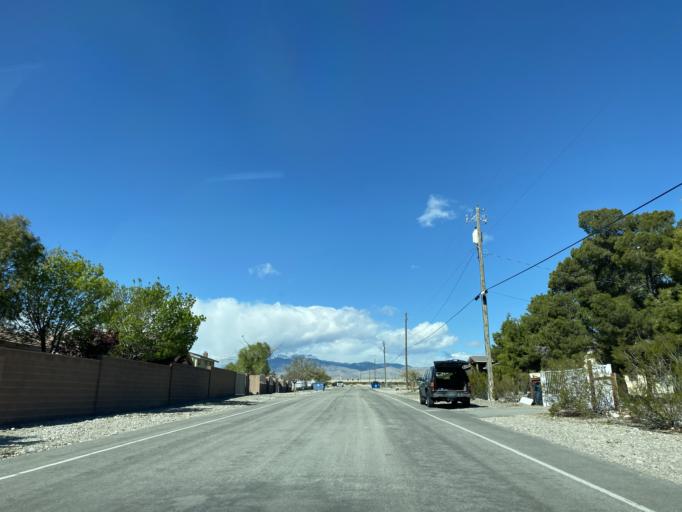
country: US
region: Nevada
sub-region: Clark County
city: North Las Vegas
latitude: 36.3320
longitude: -115.2854
